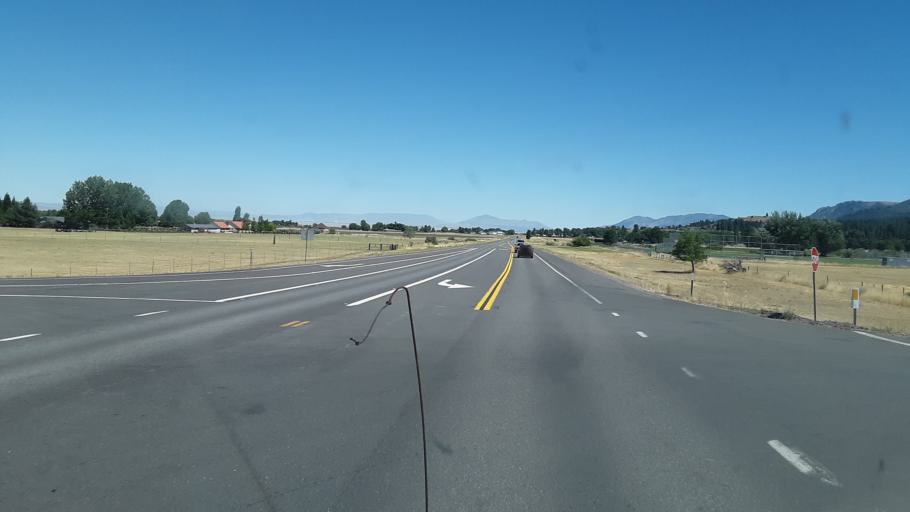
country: US
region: California
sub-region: Lassen County
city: Janesville
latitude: 40.3030
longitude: -120.5242
